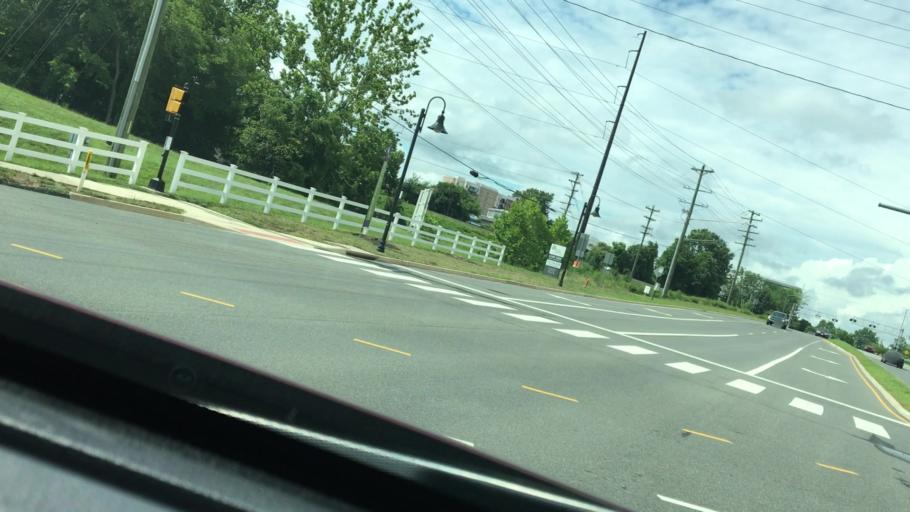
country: US
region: Virginia
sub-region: Prince William County
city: Yorkshire
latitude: 38.7626
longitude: -77.4423
